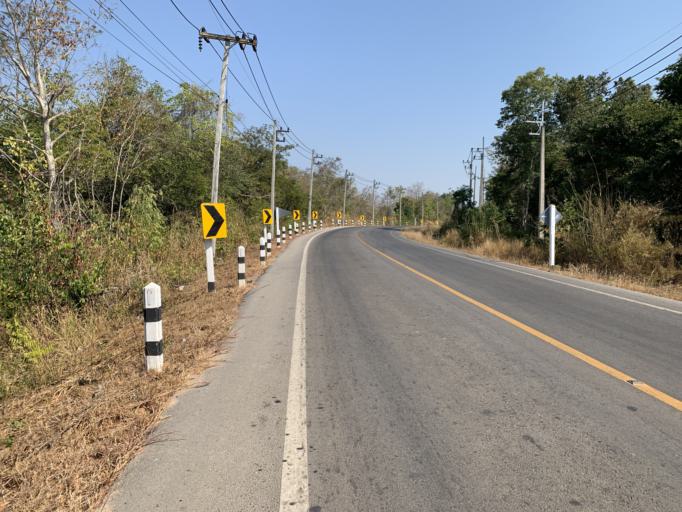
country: TH
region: Loei
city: Wang Saphung
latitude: 17.3687
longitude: 101.7210
